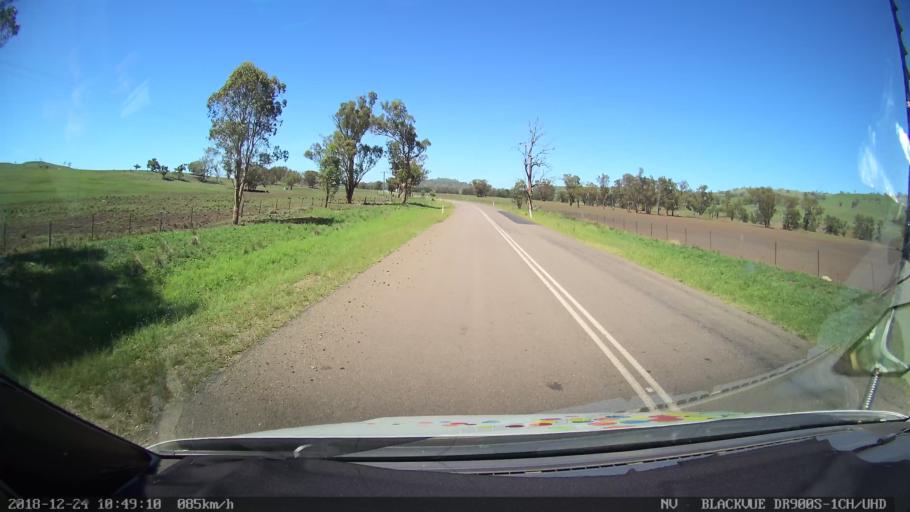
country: AU
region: New South Wales
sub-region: Upper Hunter Shire
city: Merriwa
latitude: -31.9442
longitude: 150.4288
